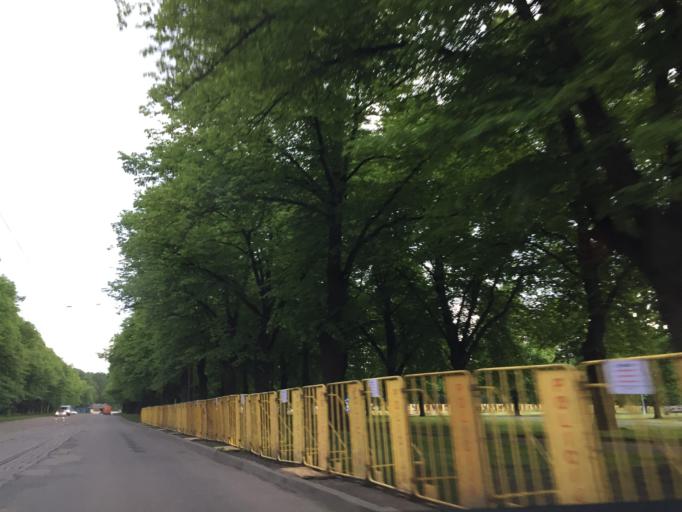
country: LV
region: Riga
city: Riga
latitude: 56.9365
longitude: 24.0876
